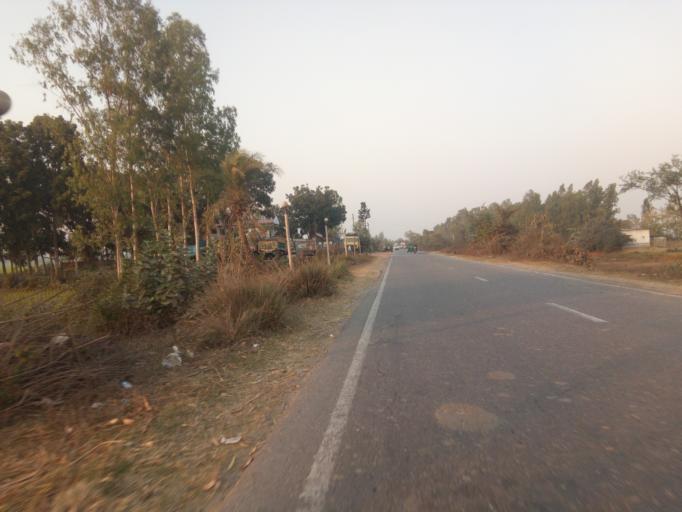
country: BD
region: Rajshahi
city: Bogra
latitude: 24.5977
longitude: 89.2383
